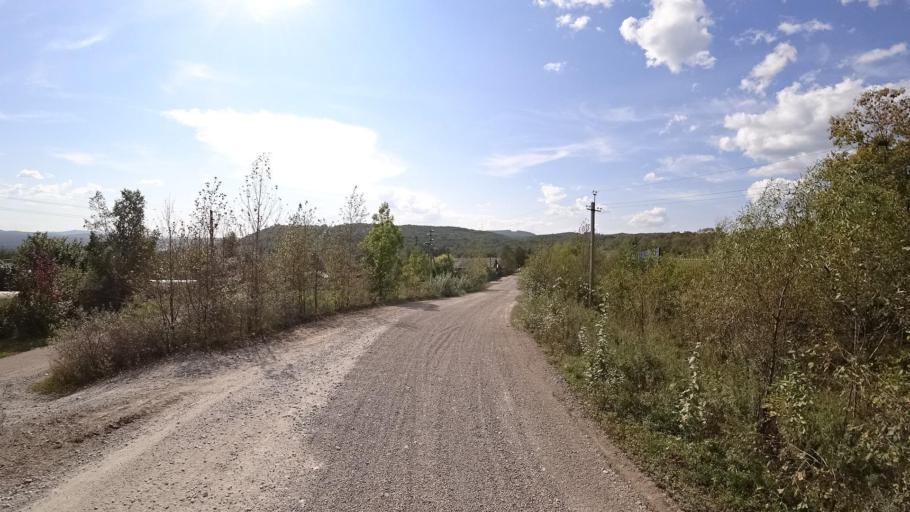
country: RU
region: Jewish Autonomous Oblast
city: Birakan
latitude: 49.0108
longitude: 131.7427
